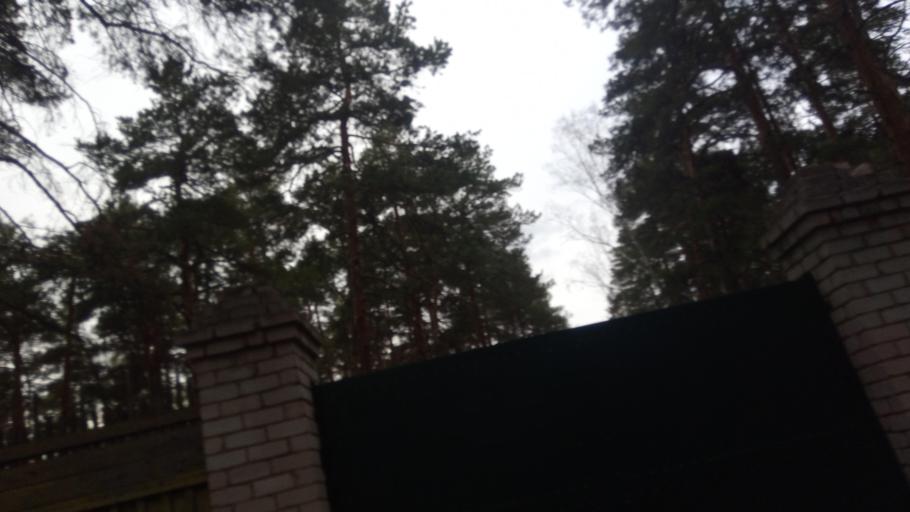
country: RU
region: Chelyabinsk
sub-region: Gorod Chelyabinsk
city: Chelyabinsk
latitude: 55.1350
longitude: 61.3446
